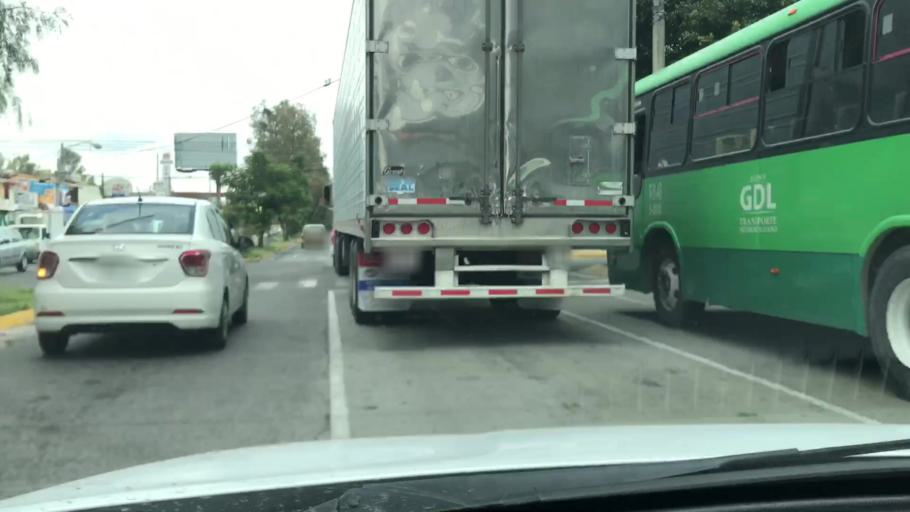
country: MX
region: Jalisco
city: Guadalajara
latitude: 20.6533
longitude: -103.4324
